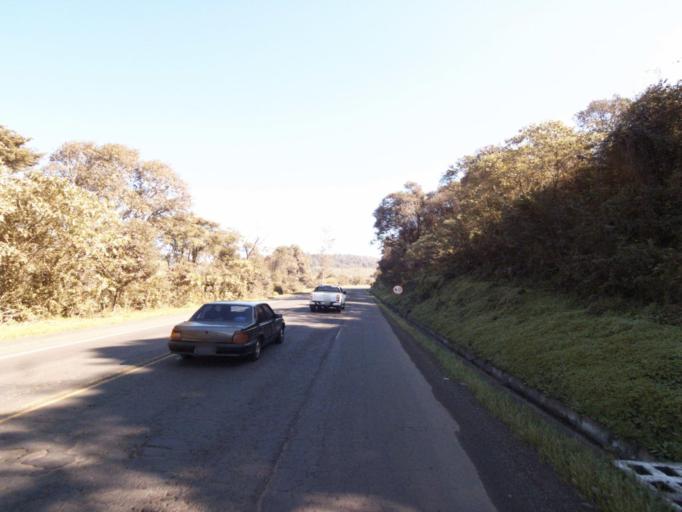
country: BR
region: Rio Grande do Sul
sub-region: Frederico Westphalen
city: Frederico Westphalen
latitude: -27.0783
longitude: -53.2278
